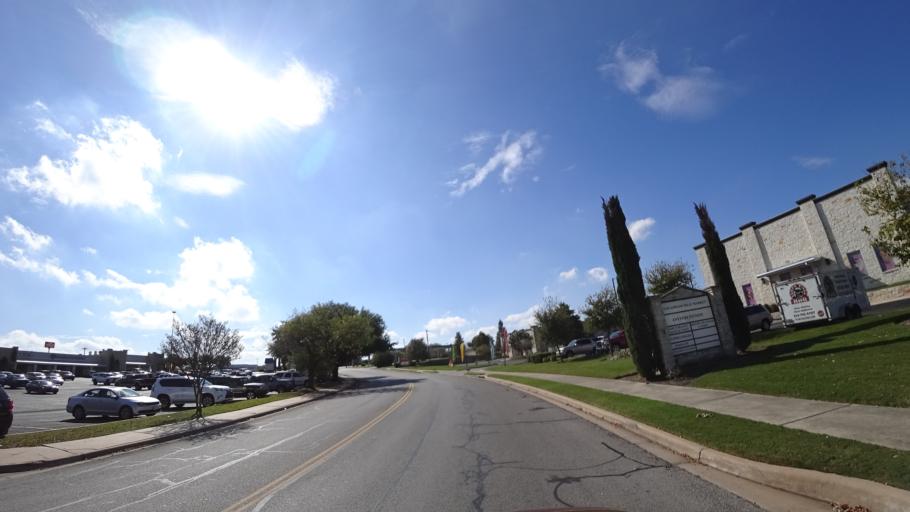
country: US
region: Texas
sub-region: Travis County
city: Windemere
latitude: 30.4478
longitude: -97.6483
